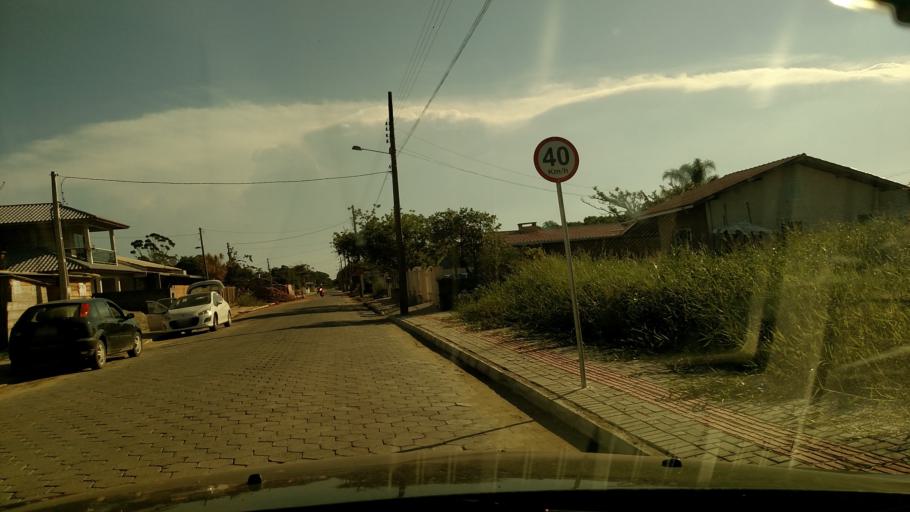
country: BR
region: Santa Catarina
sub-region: Porto Belo
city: Porto Belo
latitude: -27.1770
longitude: -48.5063
